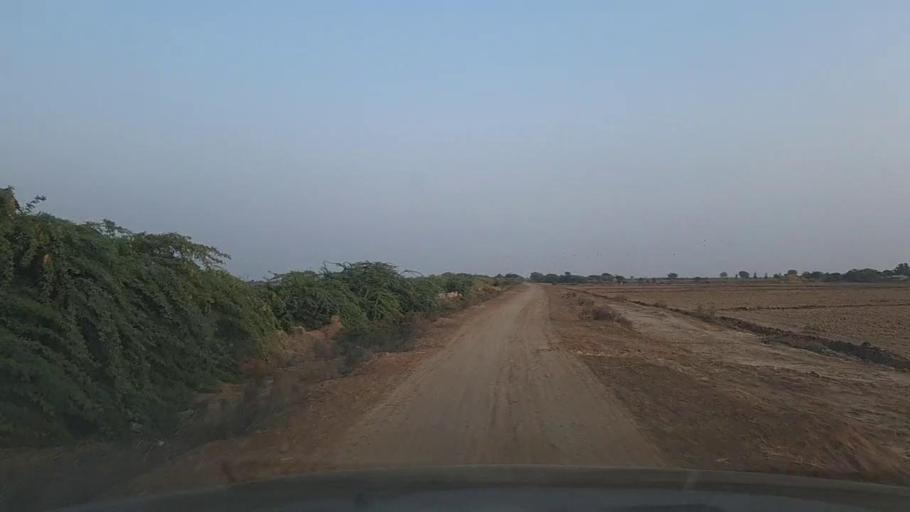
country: PK
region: Sindh
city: Jati
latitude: 24.5407
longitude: 68.3997
